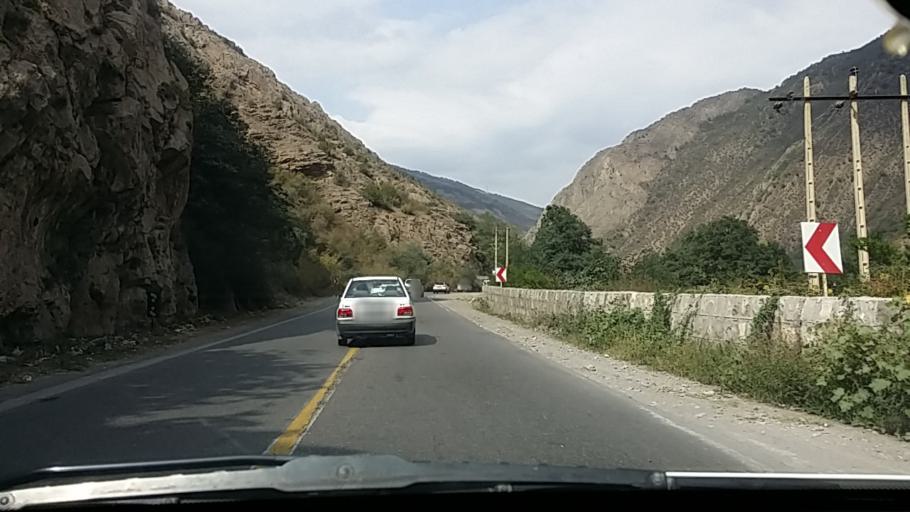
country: IR
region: Mazandaran
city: Chalus
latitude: 36.3538
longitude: 51.2613
